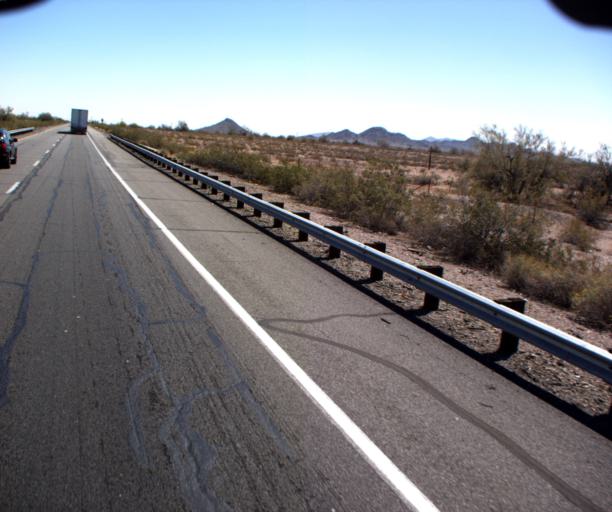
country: US
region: Arizona
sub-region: Maricopa County
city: Buckeye
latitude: 33.5191
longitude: -113.0624
